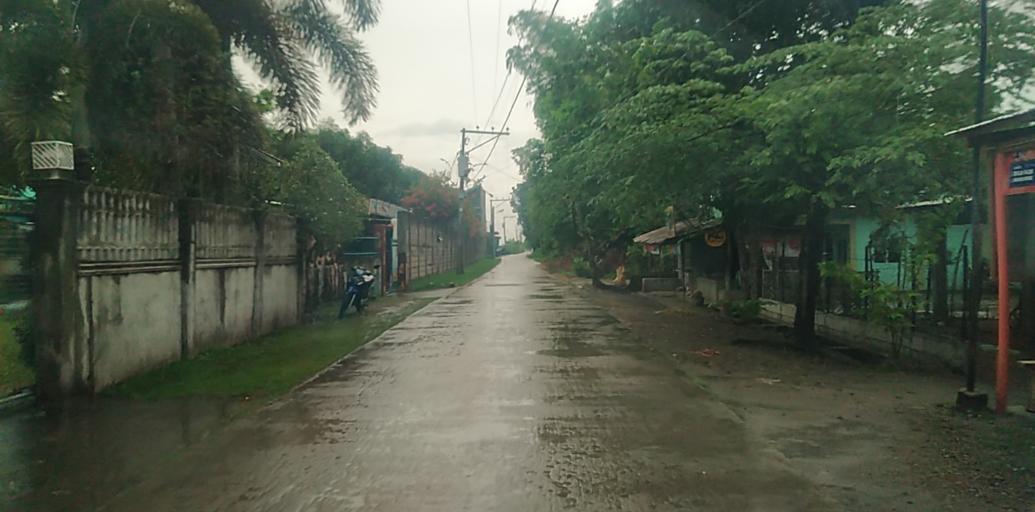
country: PH
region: Central Luzon
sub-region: Province of Pampanga
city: Panlinlang
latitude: 15.1579
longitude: 120.7211
